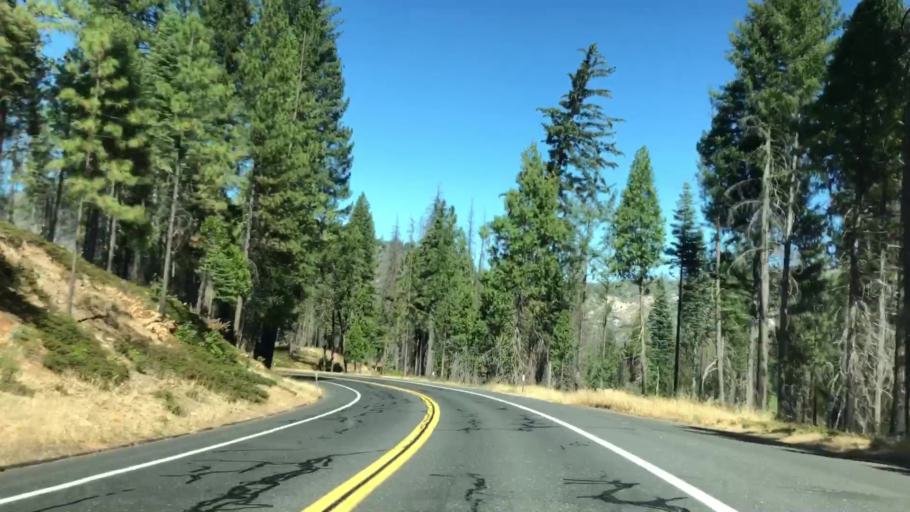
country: US
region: California
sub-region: Mariposa County
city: Midpines
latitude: 37.8135
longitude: -119.9052
